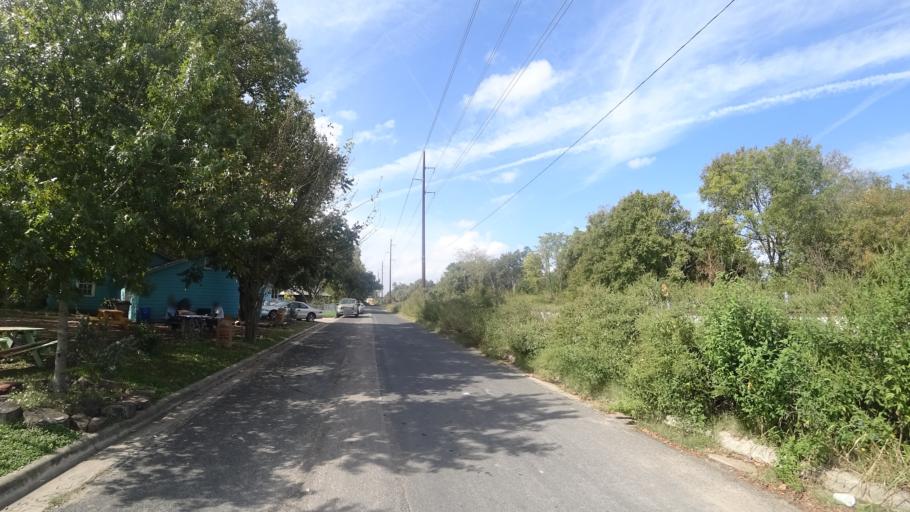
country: US
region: Texas
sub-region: Travis County
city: Austin
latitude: 30.2605
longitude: -97.7010
